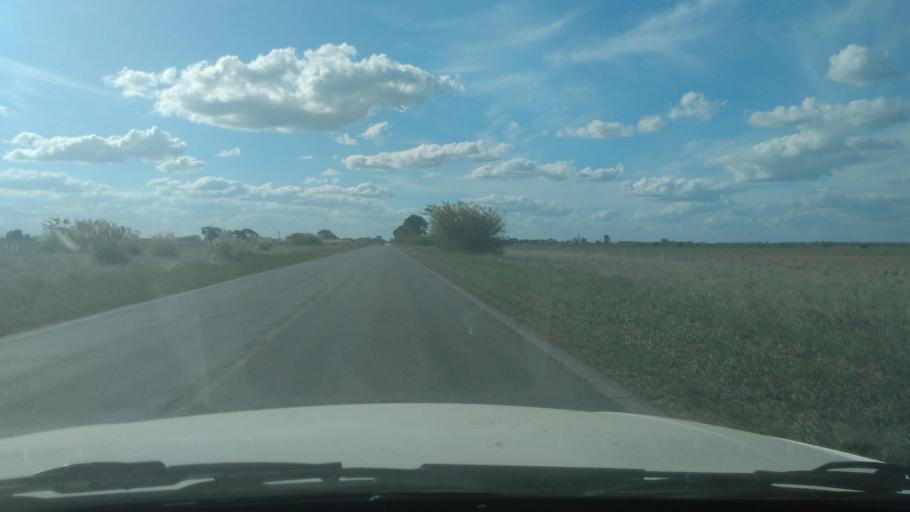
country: AR
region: Buenos Aires
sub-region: Partido de Navarro
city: Navarro
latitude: -34.9840
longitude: -59.3161
